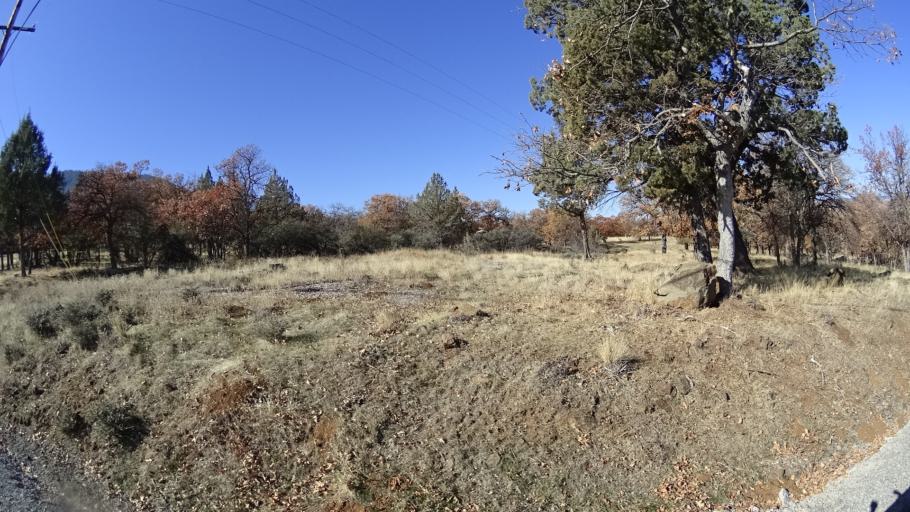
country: US
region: California
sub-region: Siskiyou County
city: Montague
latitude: 41.8779
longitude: -122.4822
